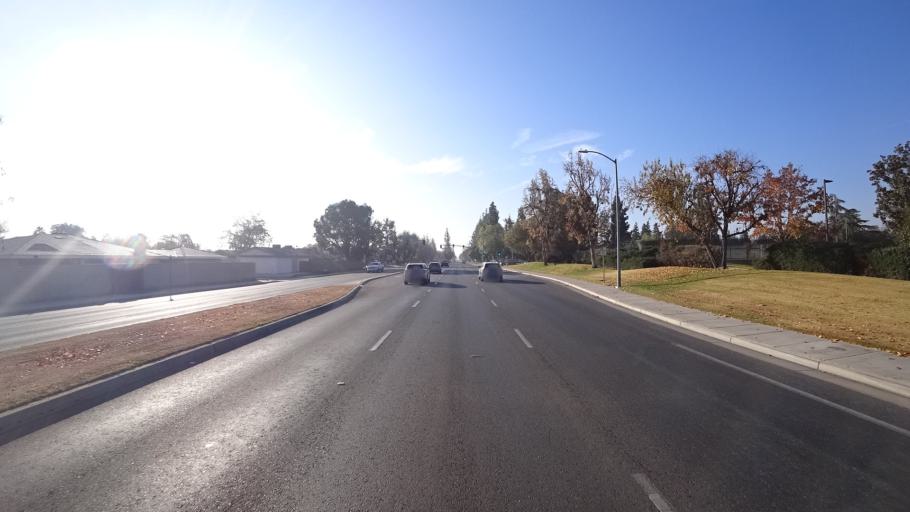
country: US
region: California
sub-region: Kern County
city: Greenacres
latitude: 35.3349
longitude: -119.0923
